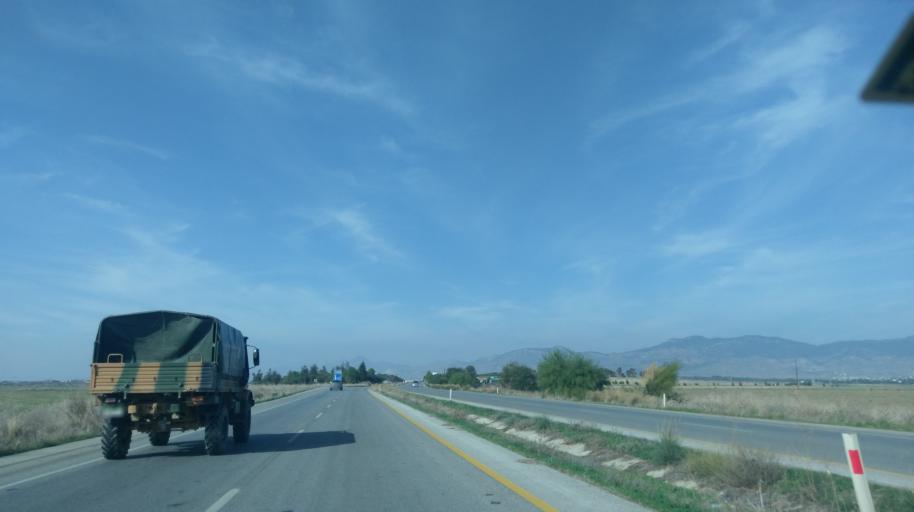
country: CY
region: Ammochostos
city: Lefkonoiko
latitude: 35.1918
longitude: 33.6243
